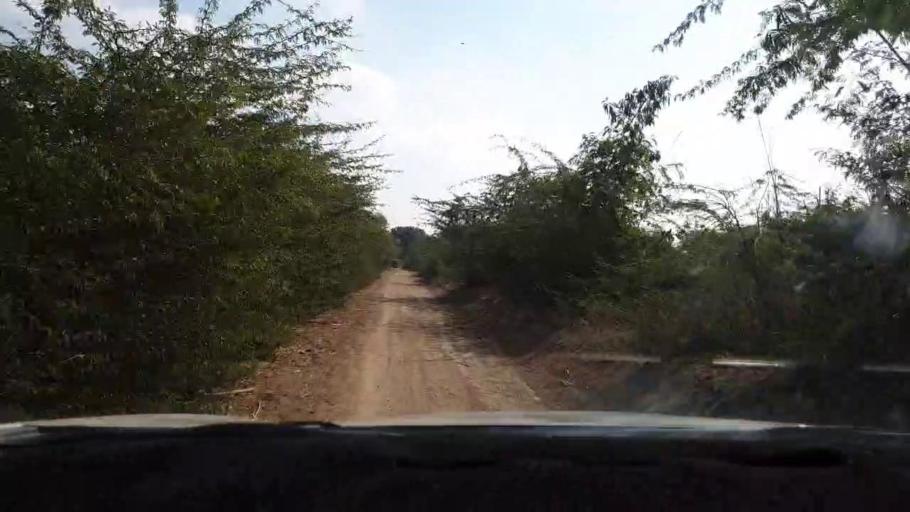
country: PK
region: Sindh
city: Berani
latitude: 25.7612
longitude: 68.9904
